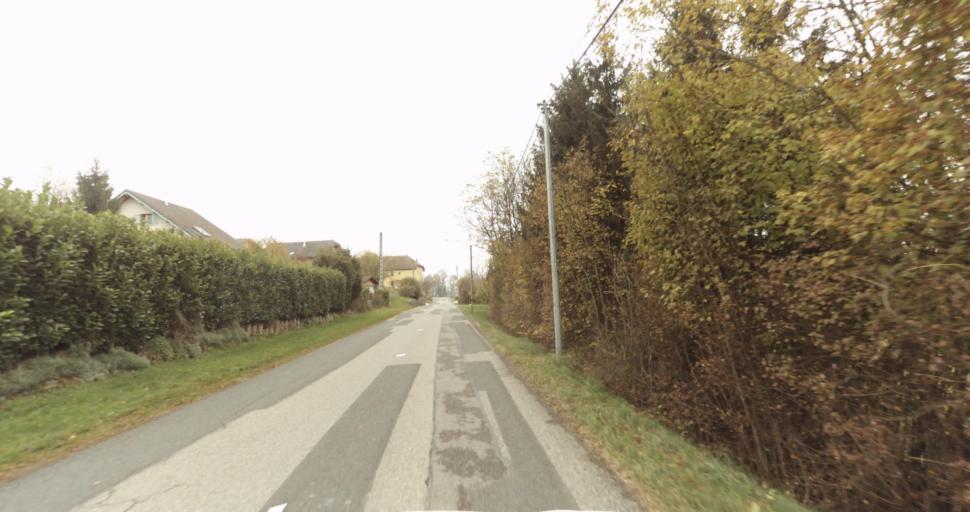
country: FR
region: Rhone-Alpes
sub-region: Departement de la Haute-Savoie
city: Gruffy
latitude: 45.7972
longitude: 6.0357
